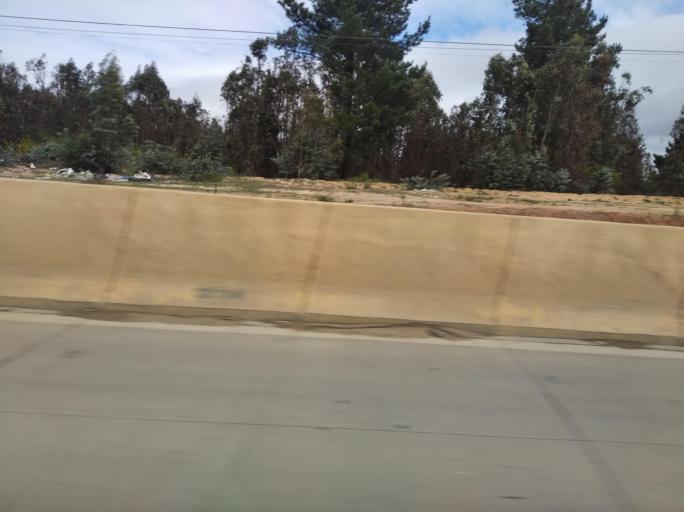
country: CL
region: Valparaiso
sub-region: Provincia de Valparaiso
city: Valparaiso
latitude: -33.0943
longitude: -71.5960
